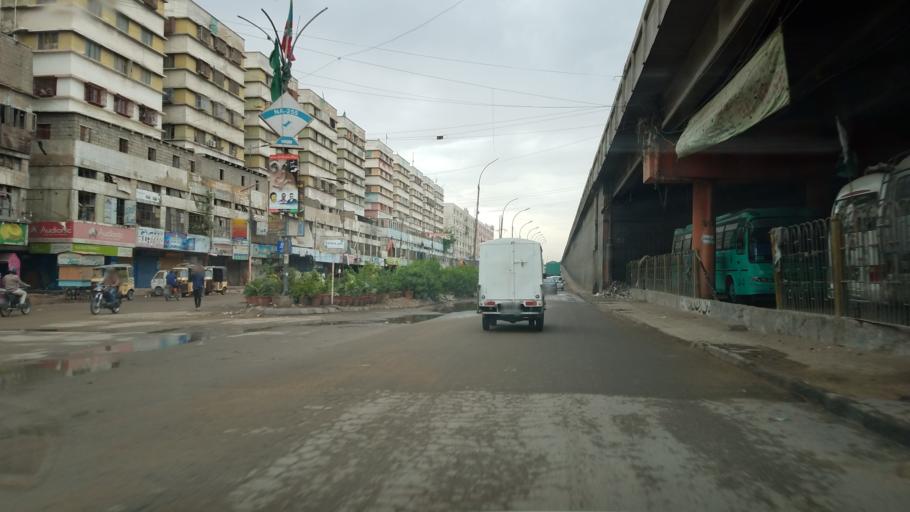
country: PK
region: Sindh
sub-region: Karachi District
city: Karachi
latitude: 24.9118
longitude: 67.0501
